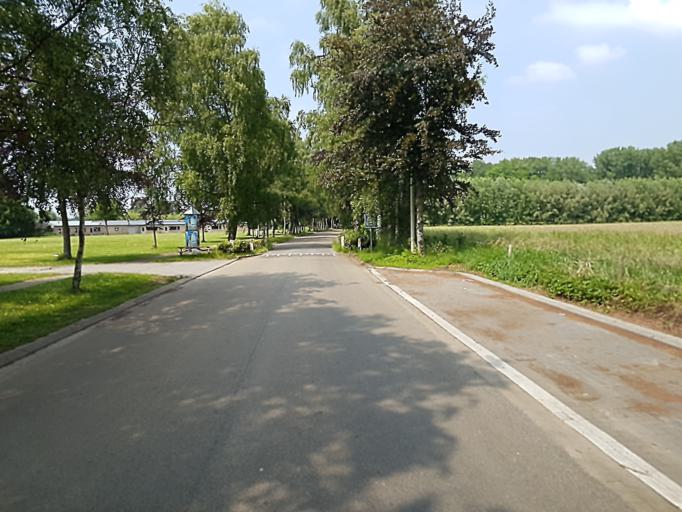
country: BE
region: Flanders
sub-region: Provincie Antwerpen
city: Ranst
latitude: 51.1940
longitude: 4.5528
